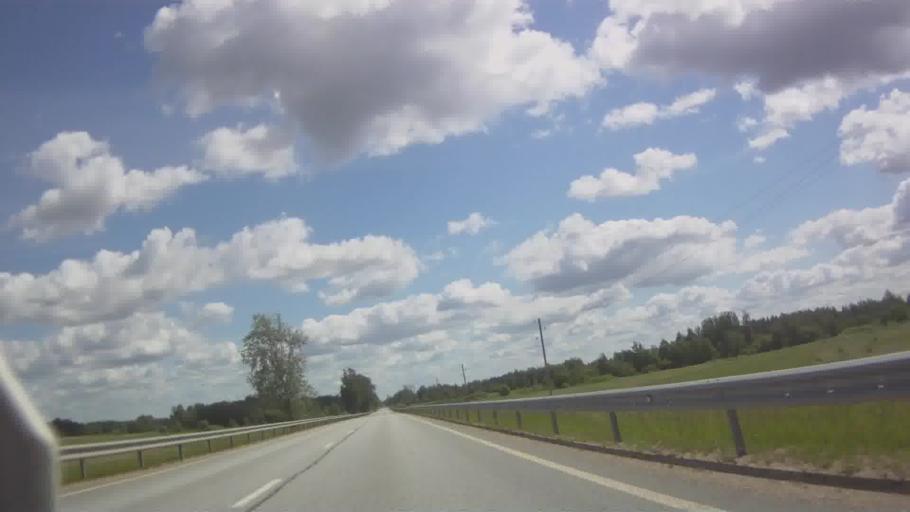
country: LV
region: Livani
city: Livani
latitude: 56.5333
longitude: 26.3275
